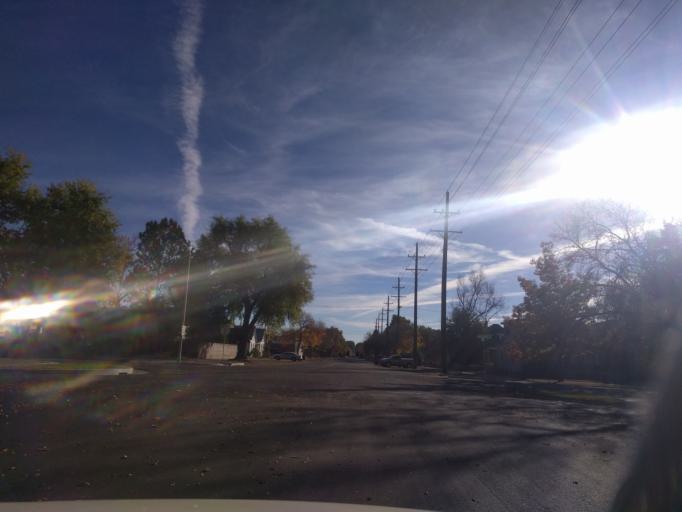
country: US
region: Colorado
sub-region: El Paso County
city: Colorado Springs
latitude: 38.8232
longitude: -104.8263
